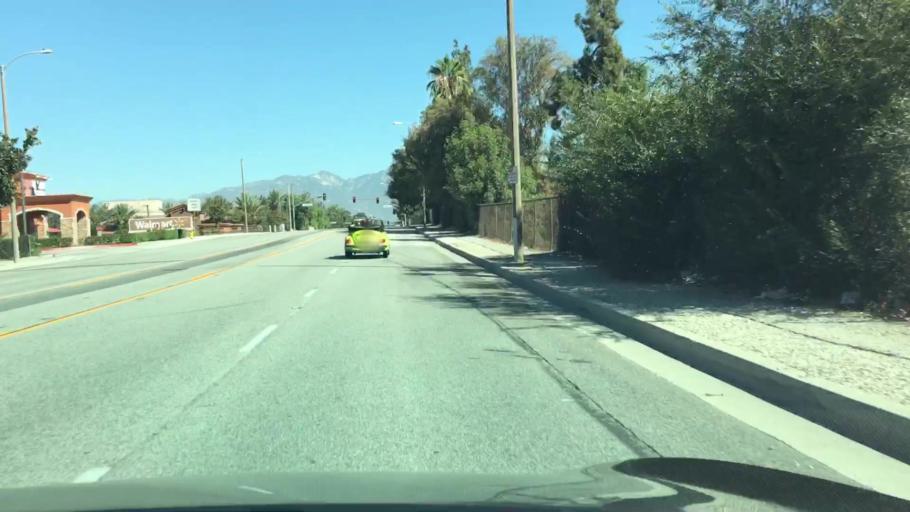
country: US
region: California
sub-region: Los Angeles County
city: South San Gabriel
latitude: 34.0488
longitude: -118.0818
